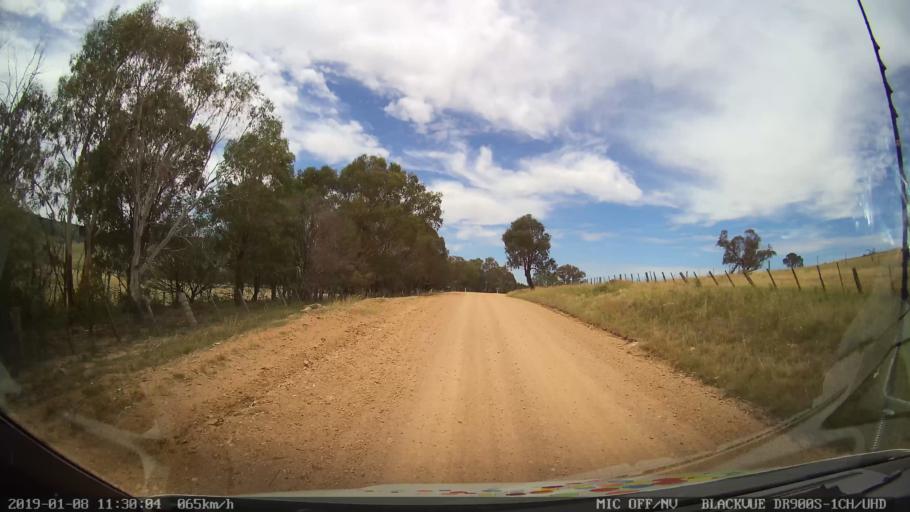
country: AU
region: New South Wales
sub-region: Guyra
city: Guyra
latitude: -30.3051
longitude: 151.5461
